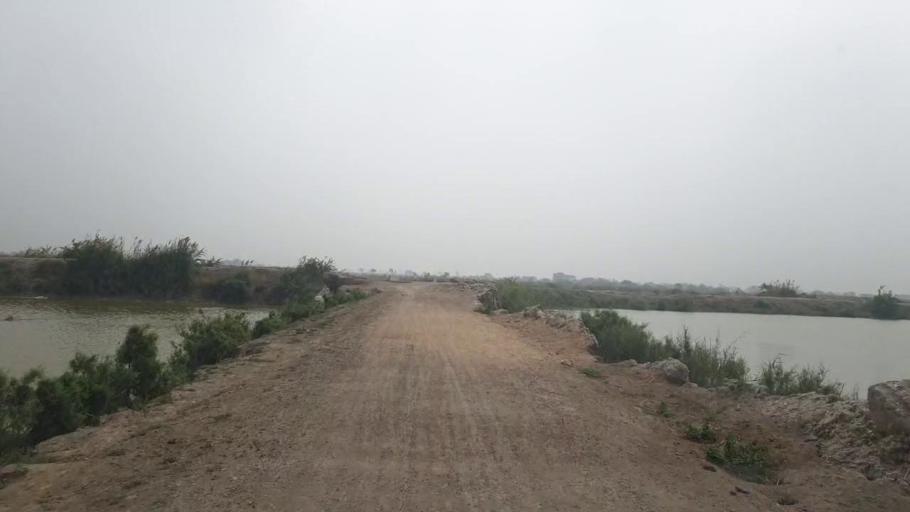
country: PK
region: Sindh
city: Badin
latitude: 24.5783
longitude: 68.6835
